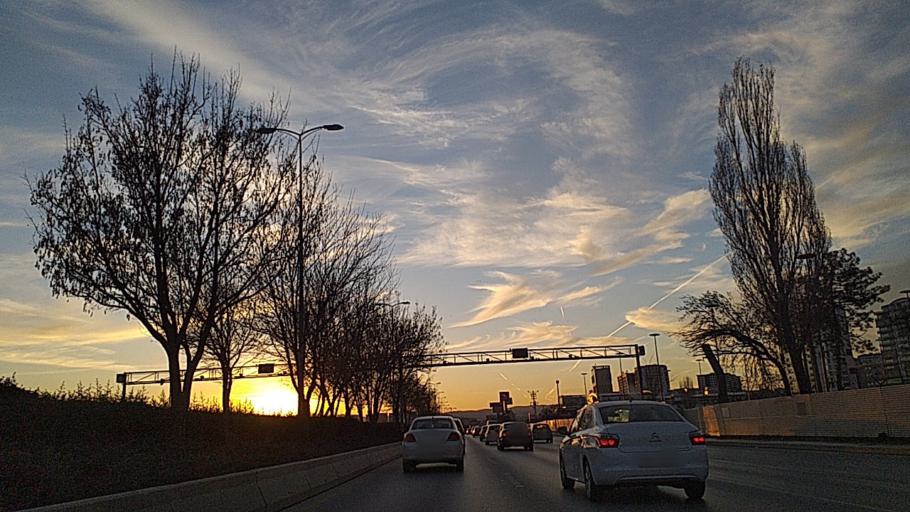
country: TR
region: Ankara
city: Etimesgut
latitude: 39.9636
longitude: 32.6502
